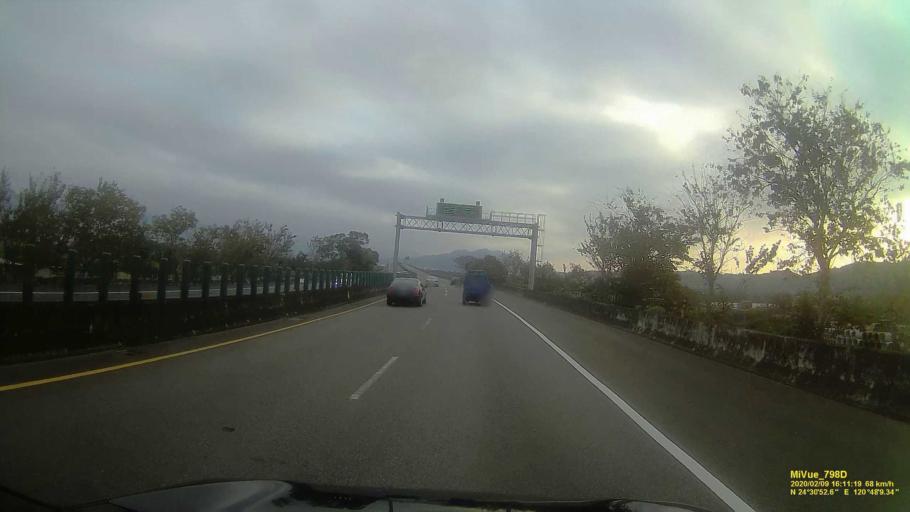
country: TW
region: Taiwan
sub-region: Miaoli
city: Miaoli
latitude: 24.5143
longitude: 120.8026
